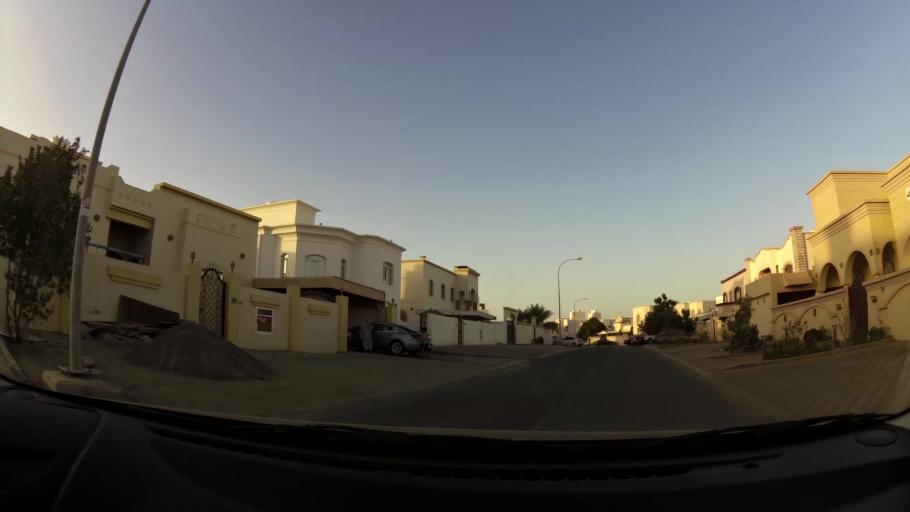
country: OM
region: Muhafazat Masqat
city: As Sib al Jadidah
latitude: 23.6033
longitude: 58.2290
